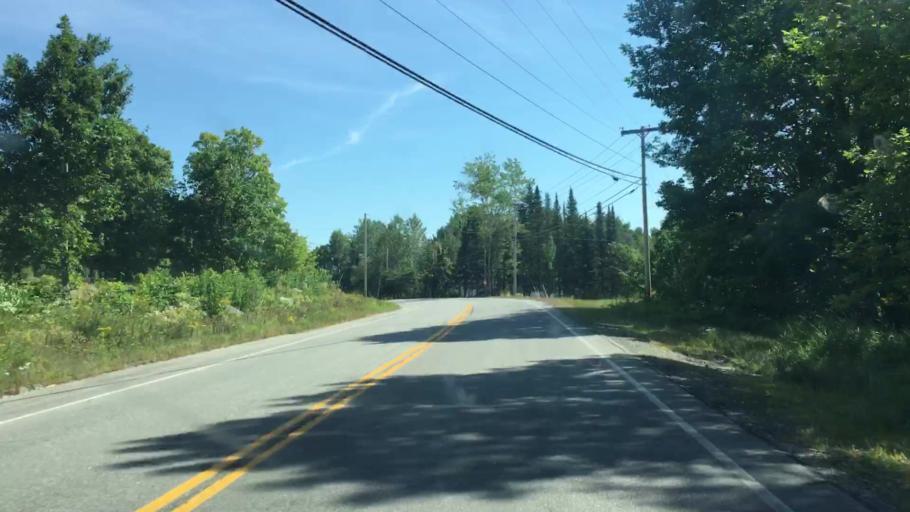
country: US
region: Maine
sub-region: Piscataquis County
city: Milo
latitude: 45.1894
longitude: -68.8962
